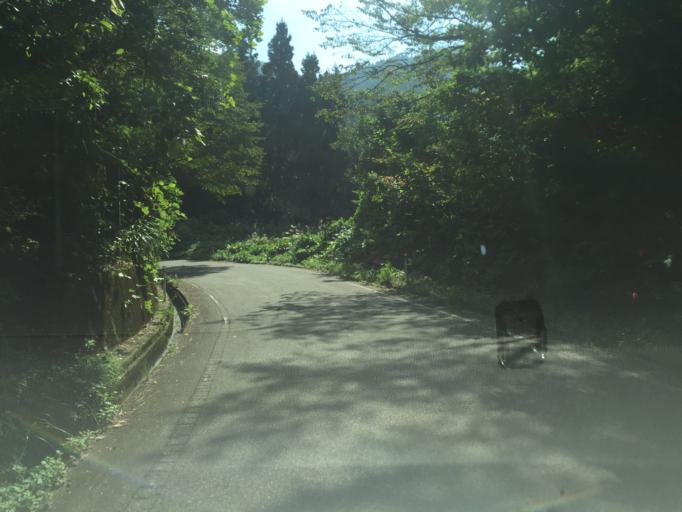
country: JP
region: Fukushima
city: Inawashiro
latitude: 37.4902
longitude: 139.9620
